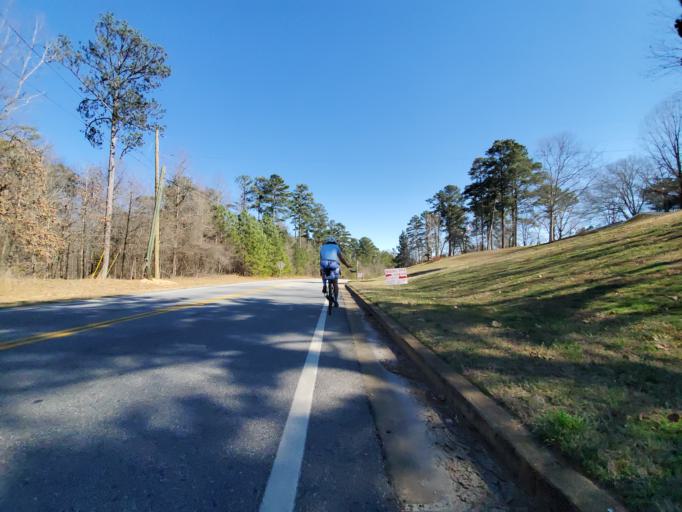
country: US
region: Georgia
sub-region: Gwinnett County
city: Lawrenceville
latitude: 33.9567
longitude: -83.9387
